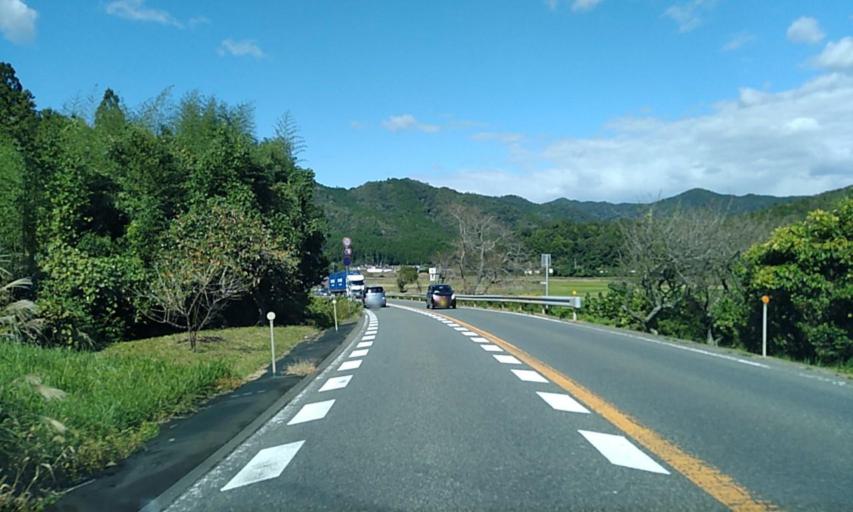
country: JP
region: Kyoto
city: Ayabe
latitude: 35.2460
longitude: 135.2116
